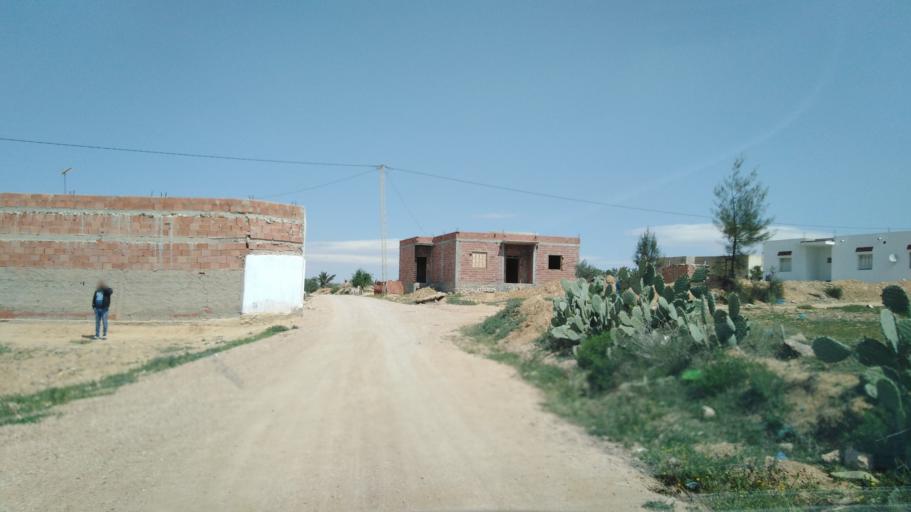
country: TN
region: Safaqis
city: Sfax
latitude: 34.7621
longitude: 10.5244
